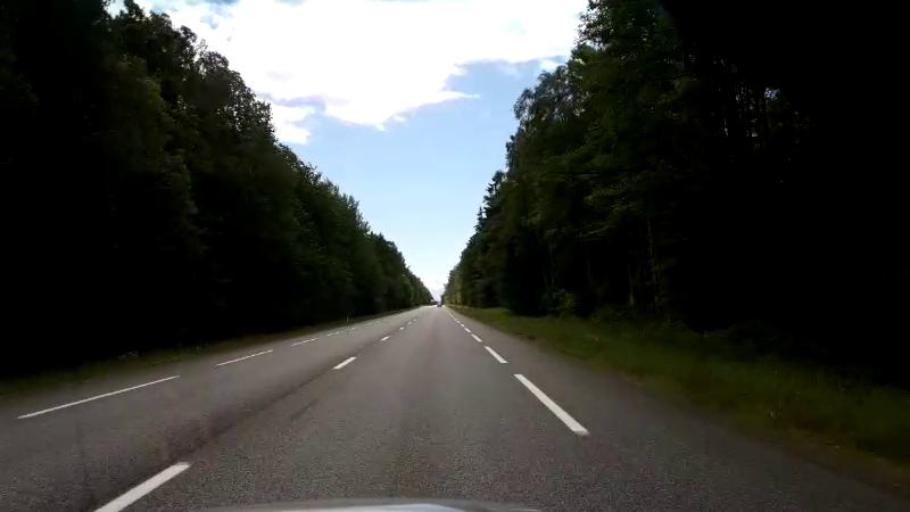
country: LV
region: Saulkrastu
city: Saulkrasti
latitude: 57.4839
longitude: 24.4328
